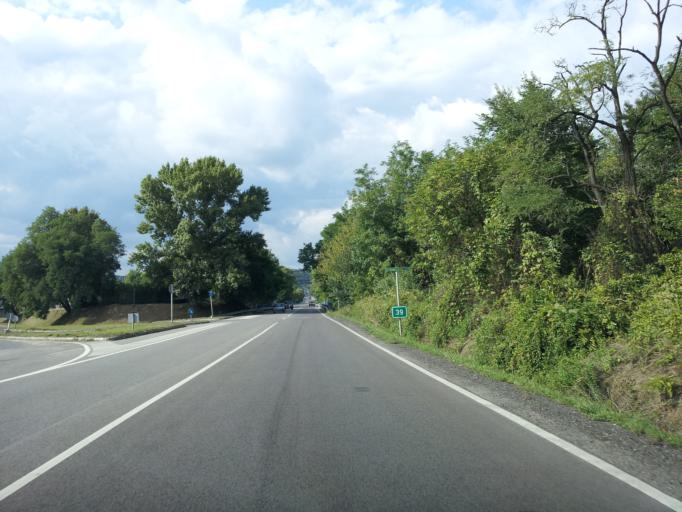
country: HU
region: Pest
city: Vac
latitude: 47.8086
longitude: 19.0948
